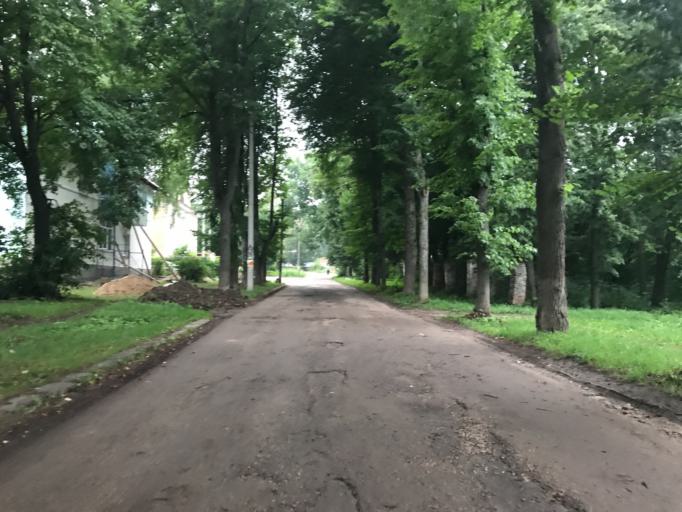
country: RU
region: Tula
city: Priupskiy
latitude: 53.9408
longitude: 37.7039
